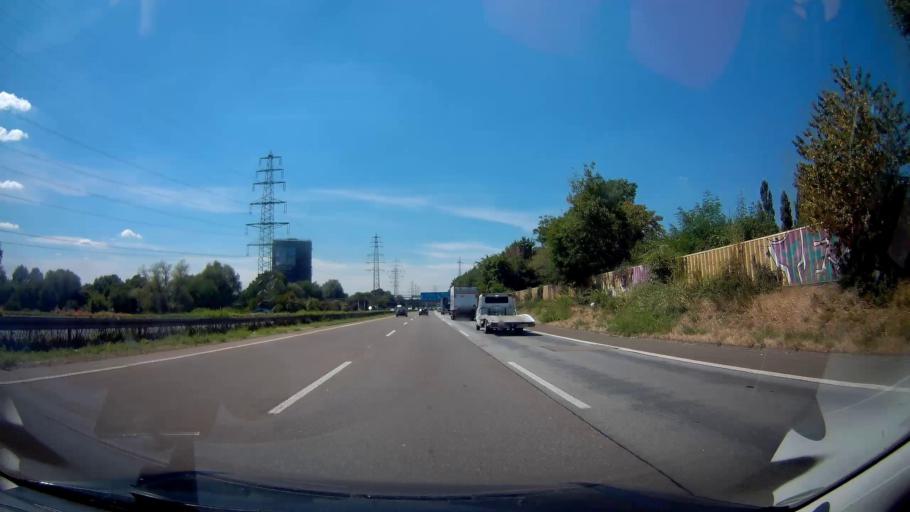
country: DE
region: North Rhine-Westphalia
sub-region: Regierungsbezirk Dusseldorf
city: Oberhausen
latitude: 51.4959
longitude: 6.8831
